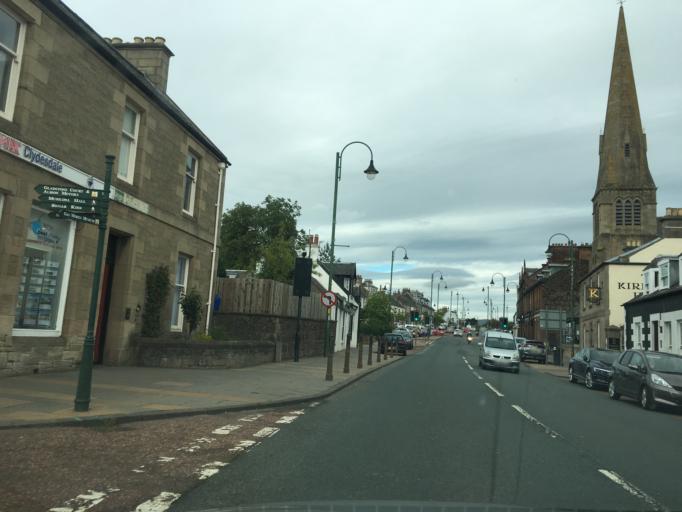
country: GB
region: Scotland
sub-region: South Lanarkshire
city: Biggar
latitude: 55.6238
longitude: -3.5255
